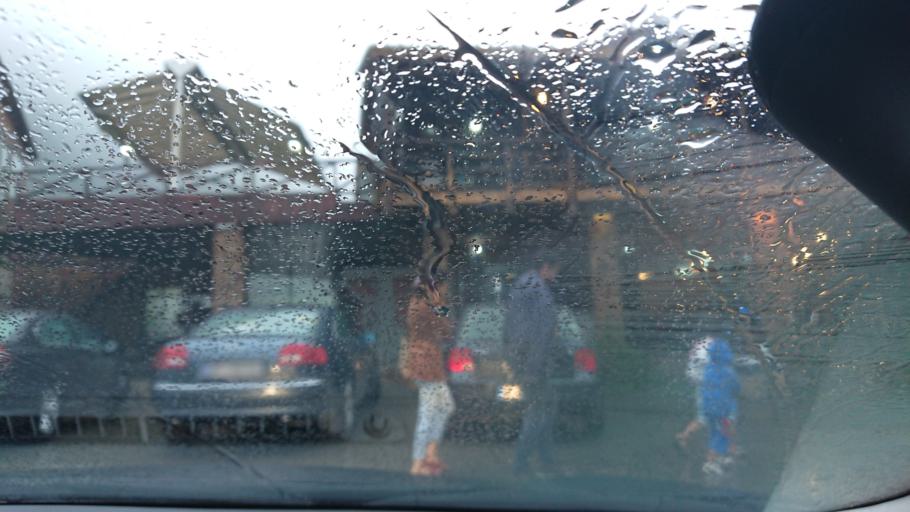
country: TR
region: Gumushane
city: Yaglidere
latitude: 40.6746
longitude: 39.4198
